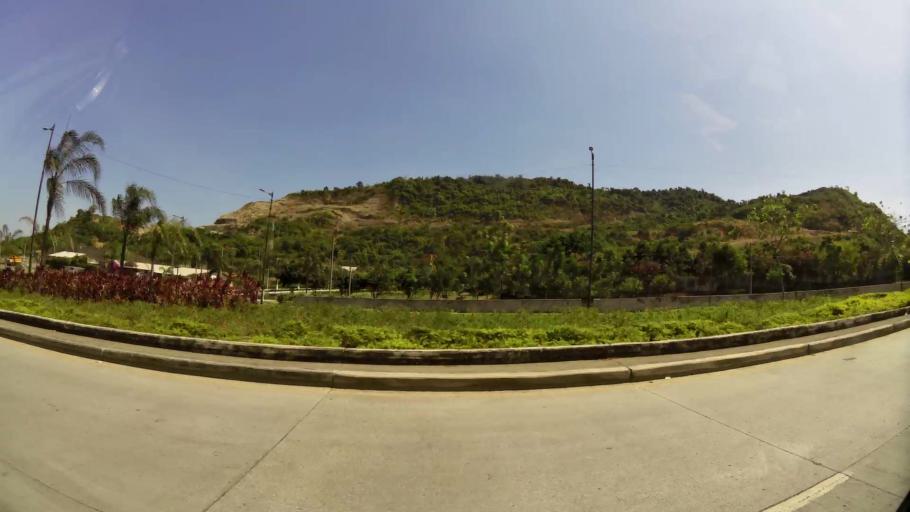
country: EC
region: Guayas
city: Guayaquil
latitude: -2.1846
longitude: -79.9319
